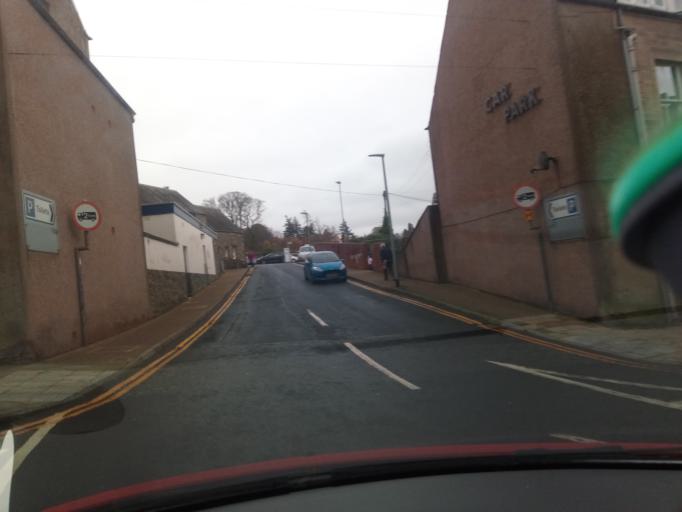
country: GB
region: Scotland
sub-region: The Scottish Borders
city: Selkirk
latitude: 55.5470
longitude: -2.8420
